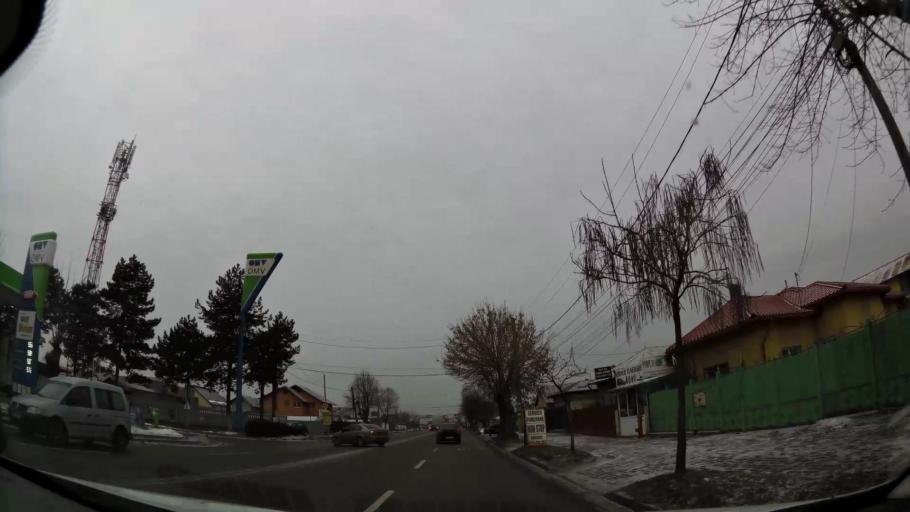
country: RO
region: Dambovita
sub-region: Comuna Ulmi
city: Ulmi
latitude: 44.9109
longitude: 25.4868
